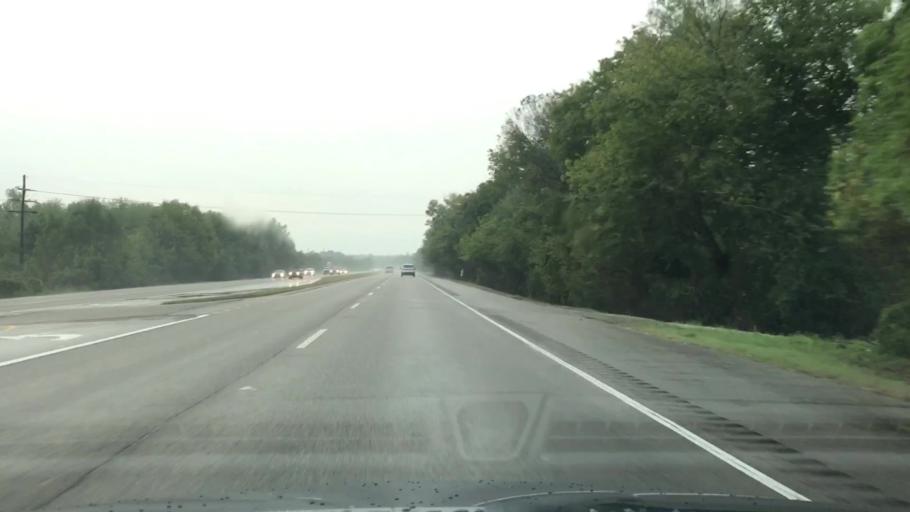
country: US
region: Louisiana
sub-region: Saint Charles Parish
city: Paradis
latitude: 29.8632
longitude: -90.4458
